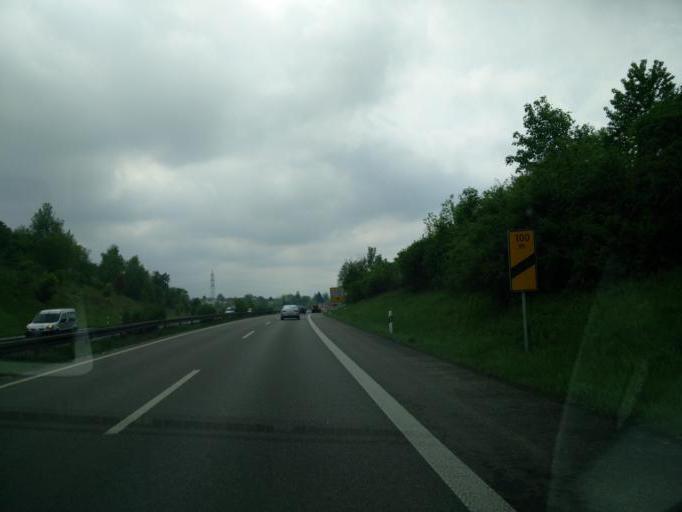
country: DE
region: Baden-Wuerttemberg
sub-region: Tuebingen Region
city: Eningen unter Achalm
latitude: 48.5093
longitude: 9.2375
